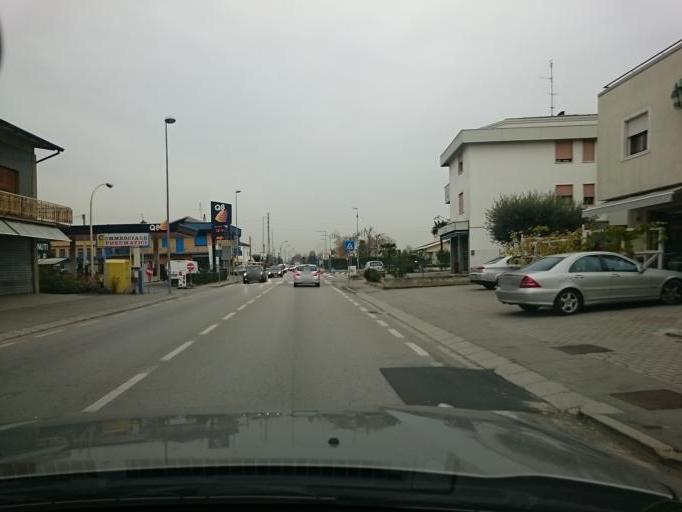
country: IT
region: Veneto
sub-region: Provincia di Padova
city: Masera di Padova
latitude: 45.3245
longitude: 11.8641
